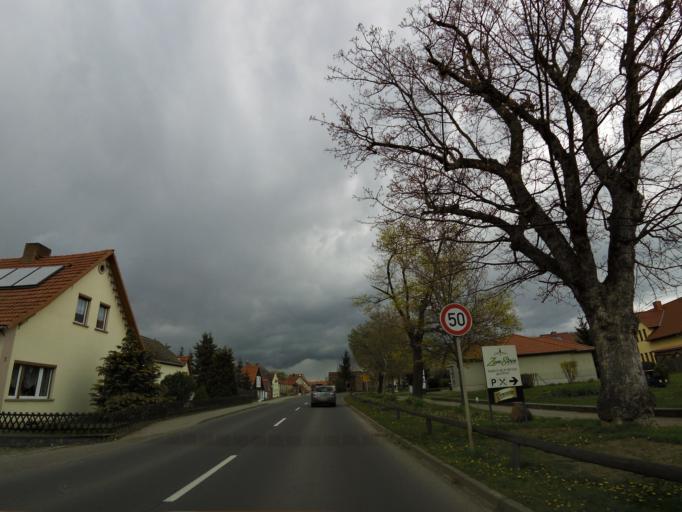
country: DE
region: Saxony-Anhalt
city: Hedersleben
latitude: 51.8555
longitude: 11.2528
